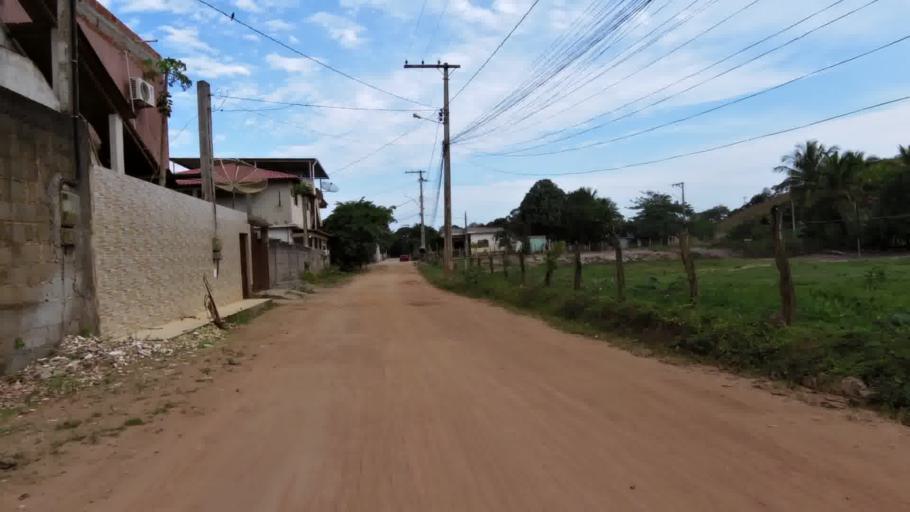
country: BR
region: Espirito Santo
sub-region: Piuma
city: Piuma
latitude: -20.8350
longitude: -40.7334
